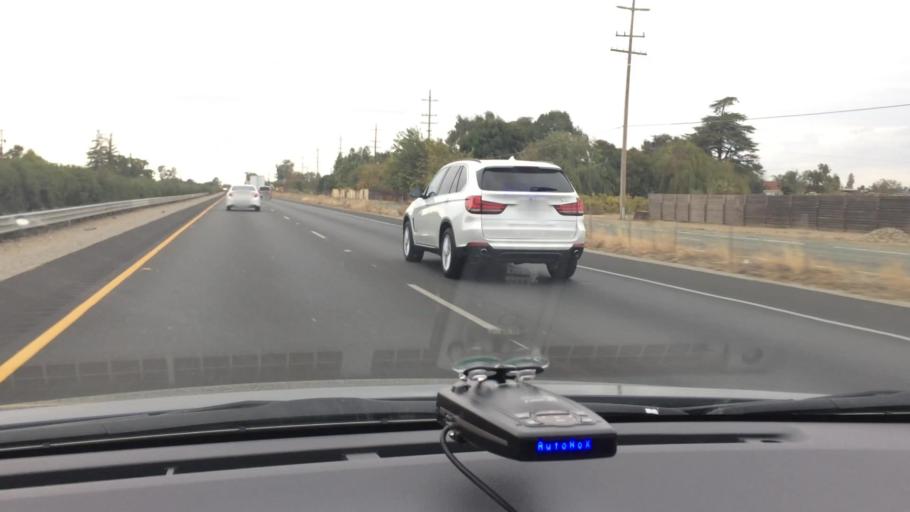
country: US
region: California
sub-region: San Joaquin County
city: Lodi
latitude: 38.1675
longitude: -121.2619
